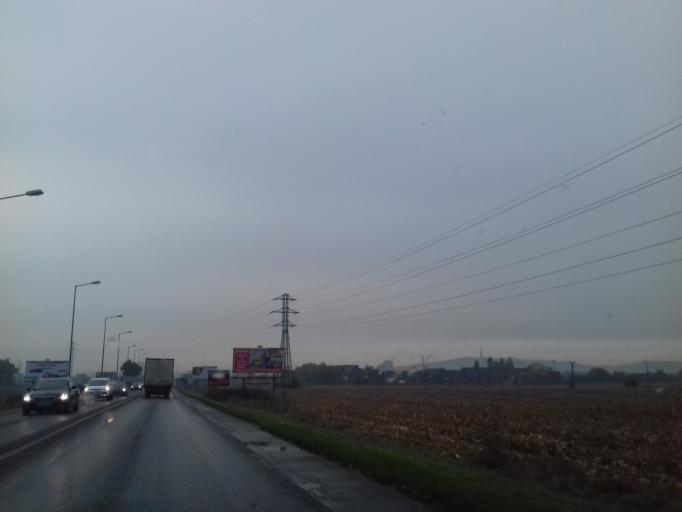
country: SK
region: Bratislavsky
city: Bratislava
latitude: 48.1336
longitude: 17.1693
